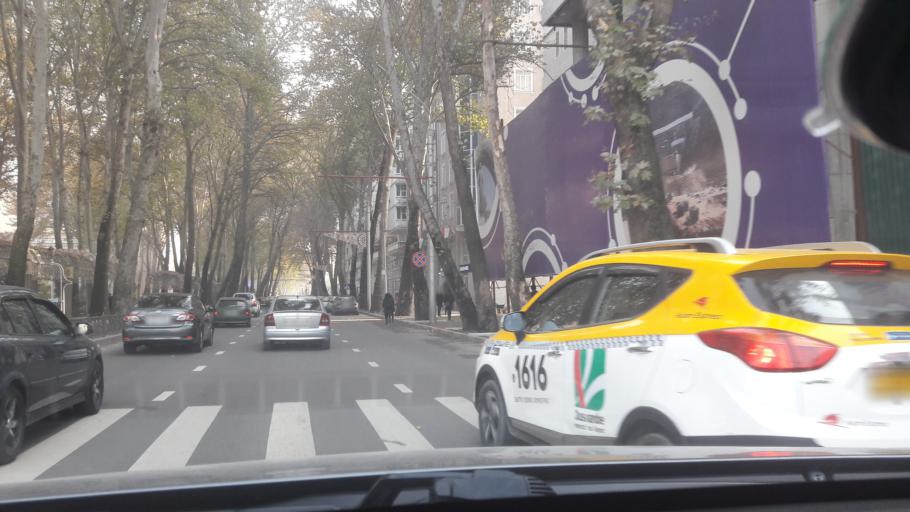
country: TJ
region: Dushanbe
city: Dushanbe
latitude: 38.5734
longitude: 68.7872
